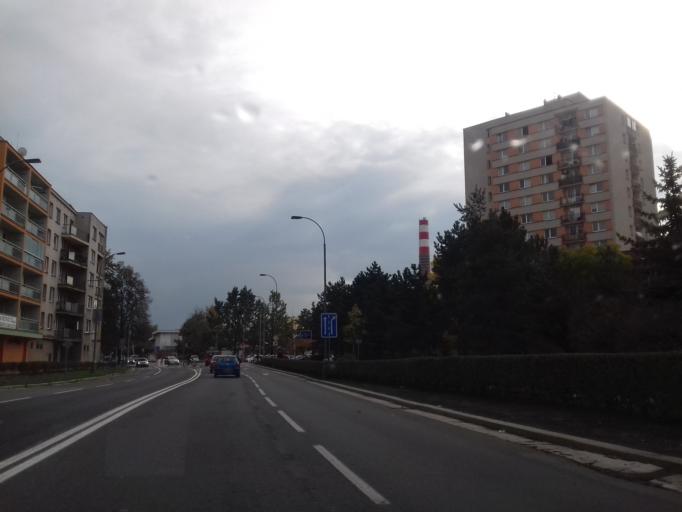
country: CZ
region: Pardubicky
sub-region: Okres Pardubice
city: Pardubice
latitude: 50.0351
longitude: 15.7798
